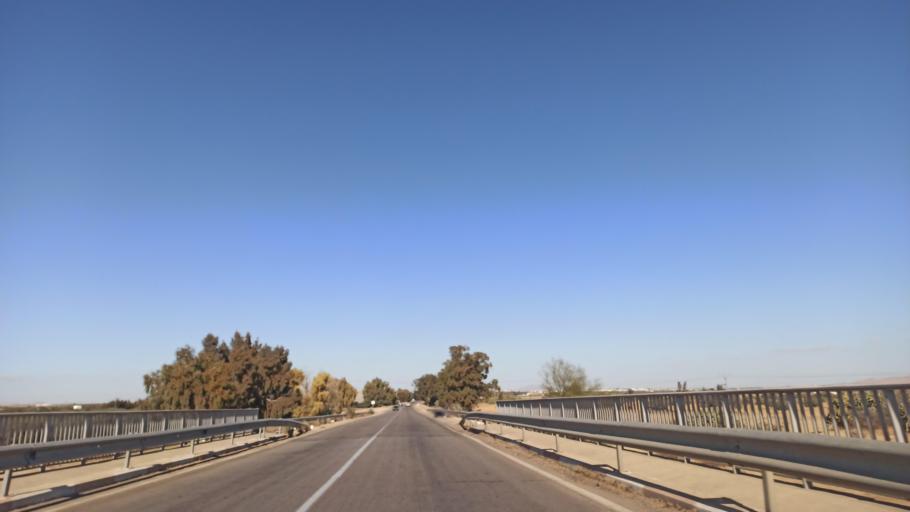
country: TN
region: Sidi Bu Zayd
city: Jilma
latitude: 35.2247
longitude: 9.3825
